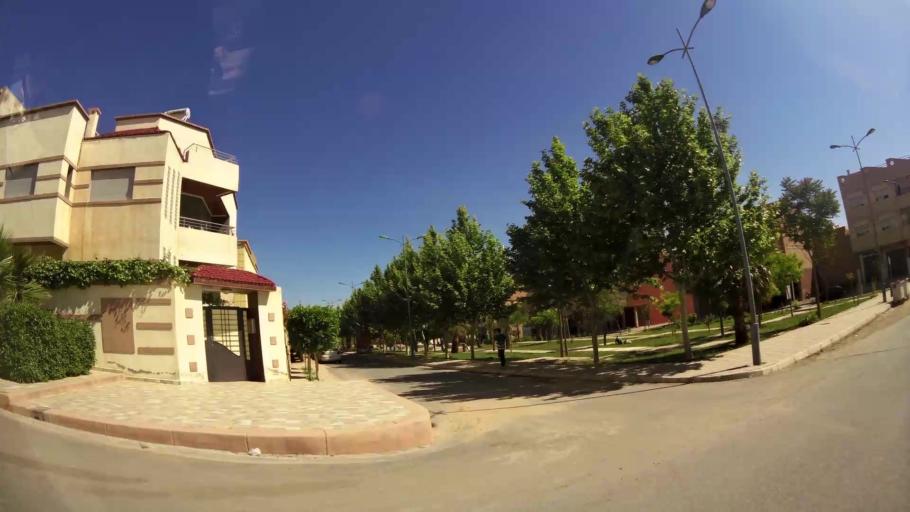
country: MA
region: Oriental
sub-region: Oujda-Angad
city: Oujda
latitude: 34.6558
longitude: -1.8849
